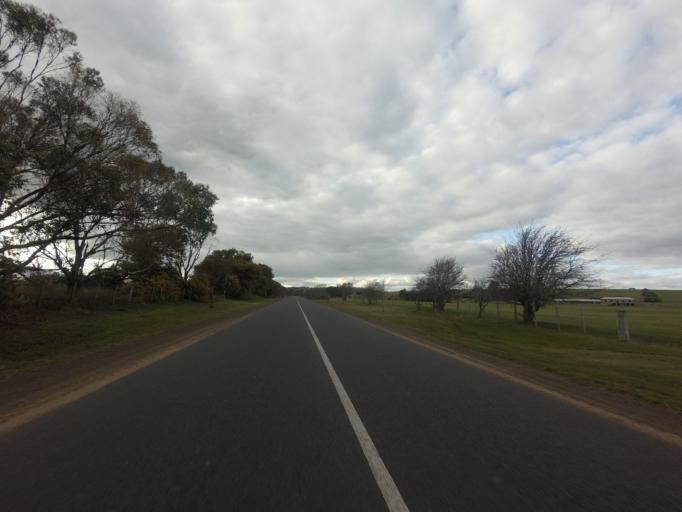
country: AU
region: Tasmania
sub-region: Northern Midlands
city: Evandale
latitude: -42.0215
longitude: 147.4925
